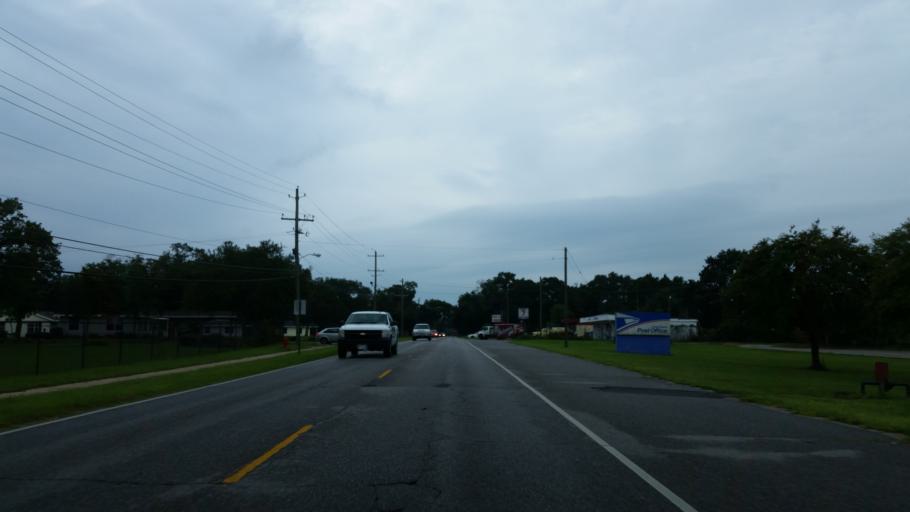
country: US
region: Florida
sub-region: Escambia County
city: Warrington
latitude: 30.3957
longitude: -87.2734
